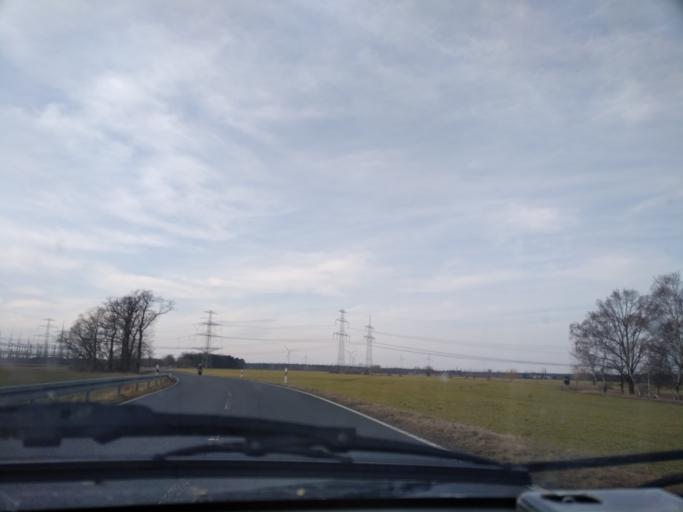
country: DE
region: Saxony-Anhalt
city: Holzdorf
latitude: 51.8266
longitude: 13.1636
